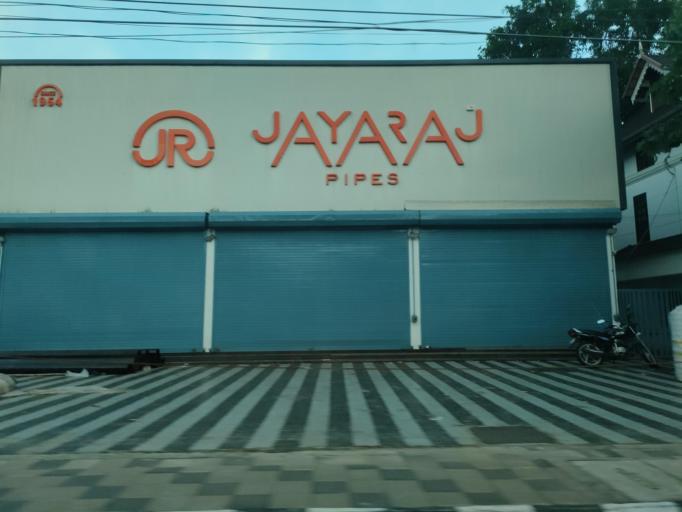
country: IN
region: Kerala
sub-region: Kozhikode
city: Kozhikode
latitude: 11.2637
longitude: 75.7715
